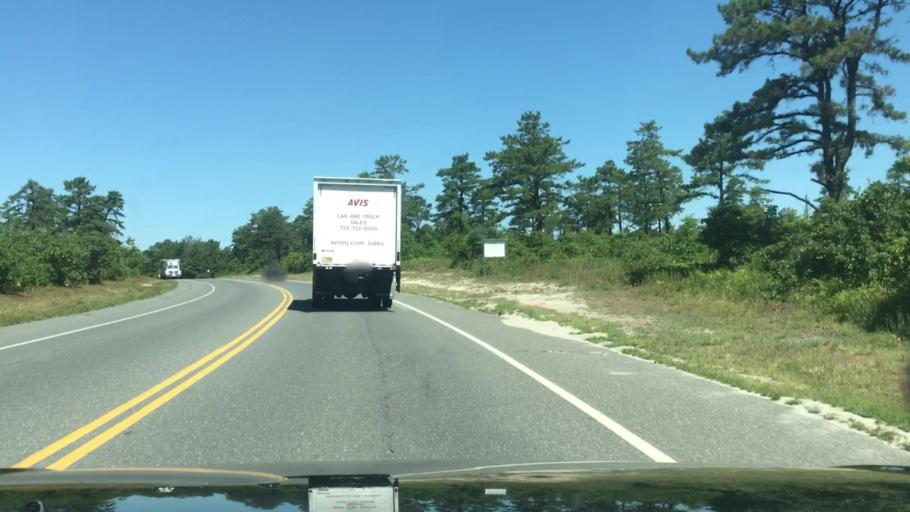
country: US
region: New Jersey
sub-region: Ocean County
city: Holiday City South
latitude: 39.9390
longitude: -74.2333
